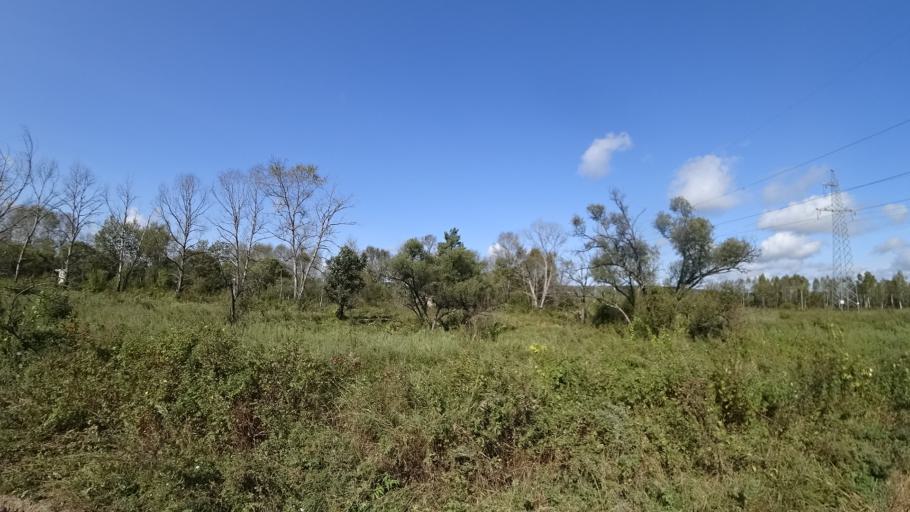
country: RU
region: Amur
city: Arkhara
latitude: 49.4088
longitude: 130.1612
